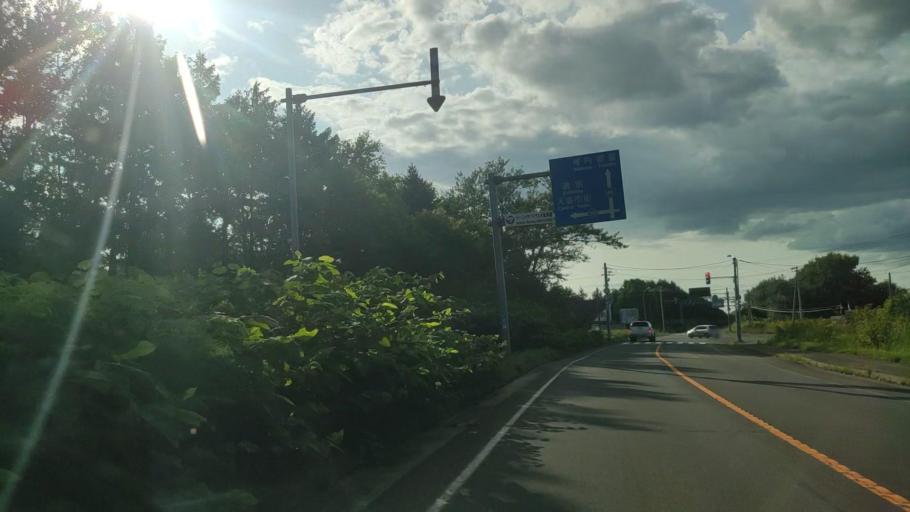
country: JP
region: Hokkaido
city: Makubetsu
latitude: 44.8974
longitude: 141.9169
